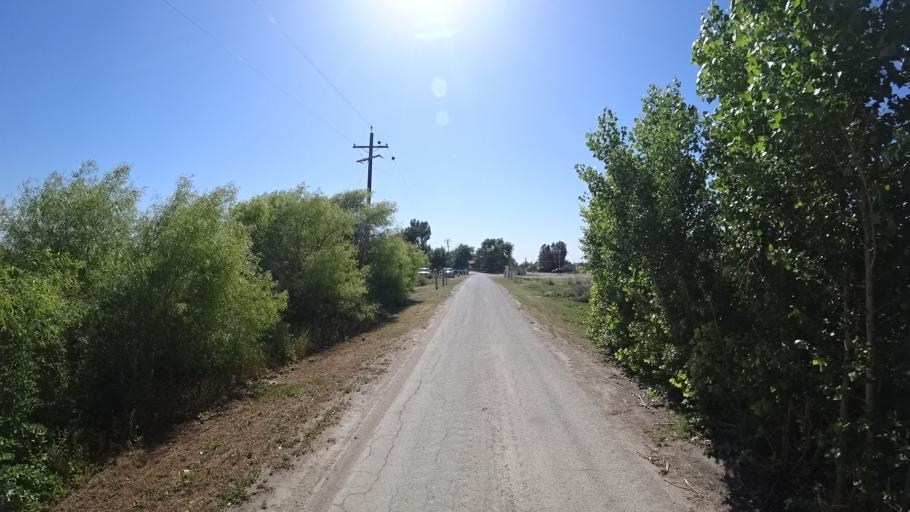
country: US
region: California
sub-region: Kings County
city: Lemoore Station
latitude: 36.2496
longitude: -119.8567
